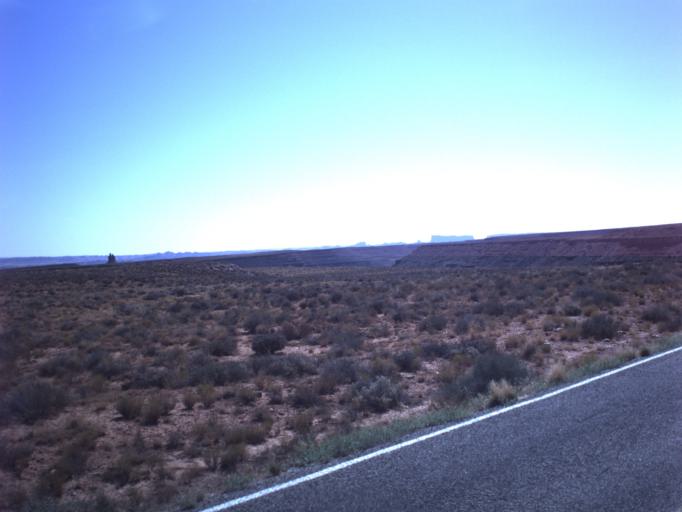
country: US
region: Arizona
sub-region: Navajo County
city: Kayenta
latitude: 37.1899
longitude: -109.9127
